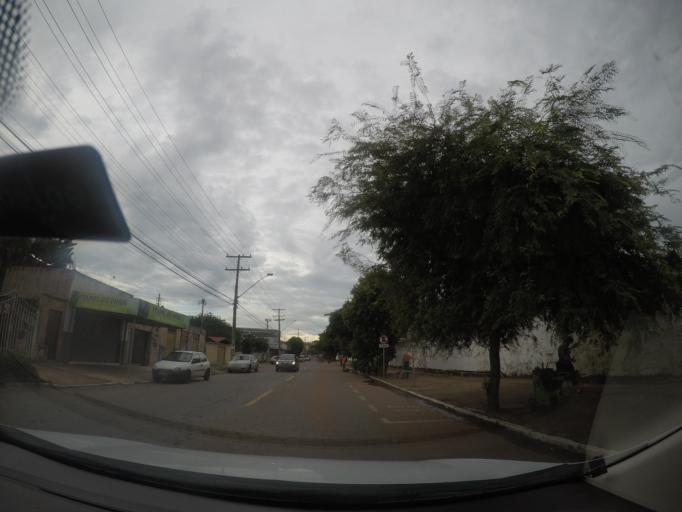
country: BR
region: Goias
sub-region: Goiania
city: Goiania
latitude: -16.6567
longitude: -49.2520
